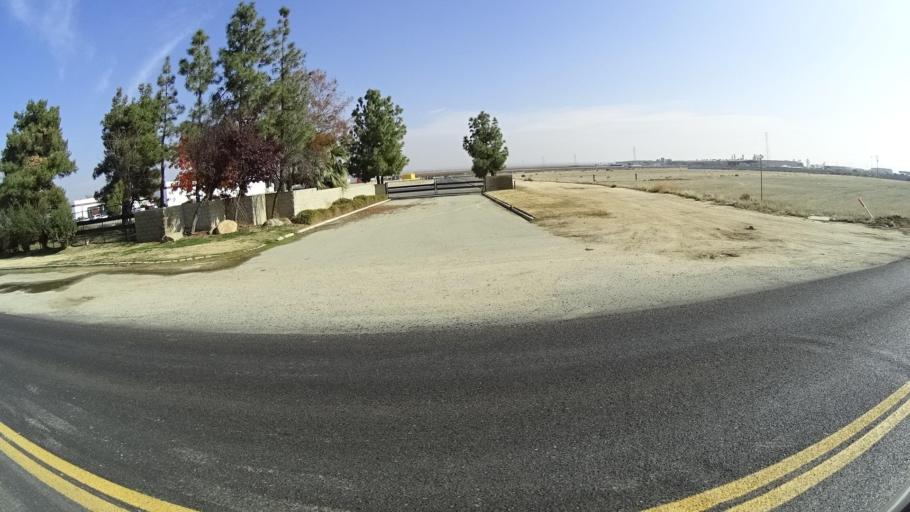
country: US
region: California
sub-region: Kern County
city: Shafter
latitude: 35.5047
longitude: -119.1525
